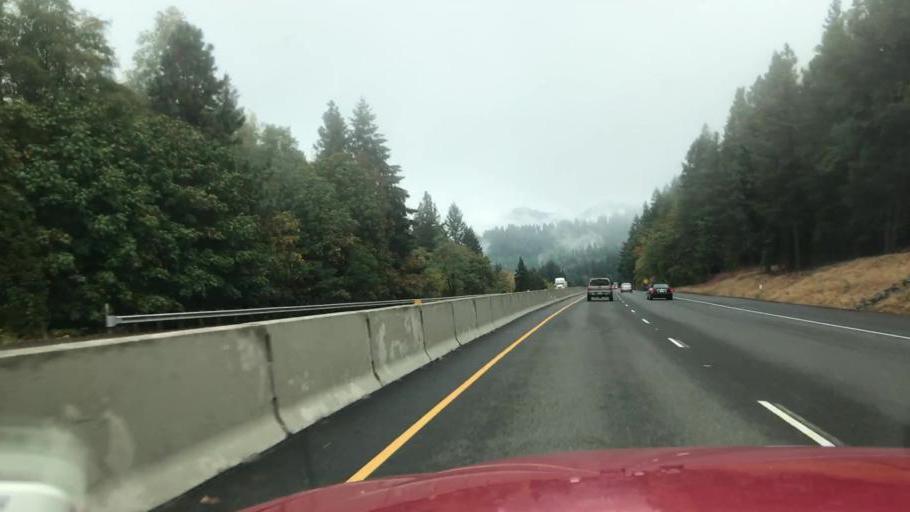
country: US
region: Oregon
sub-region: Josephine County
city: Merlin
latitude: 42.6054
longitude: -123.3830
